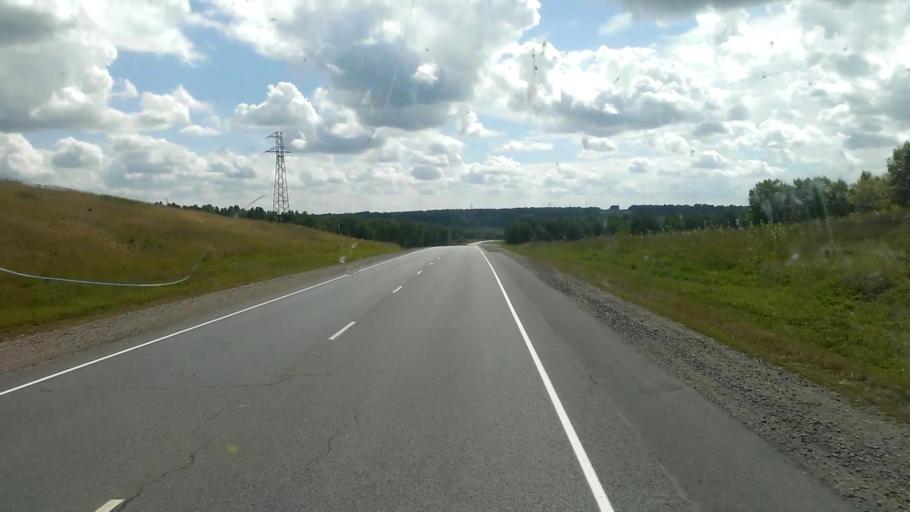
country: RU
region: Altai Krai
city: Troitskoye
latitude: 52.9440
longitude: 84.7760
